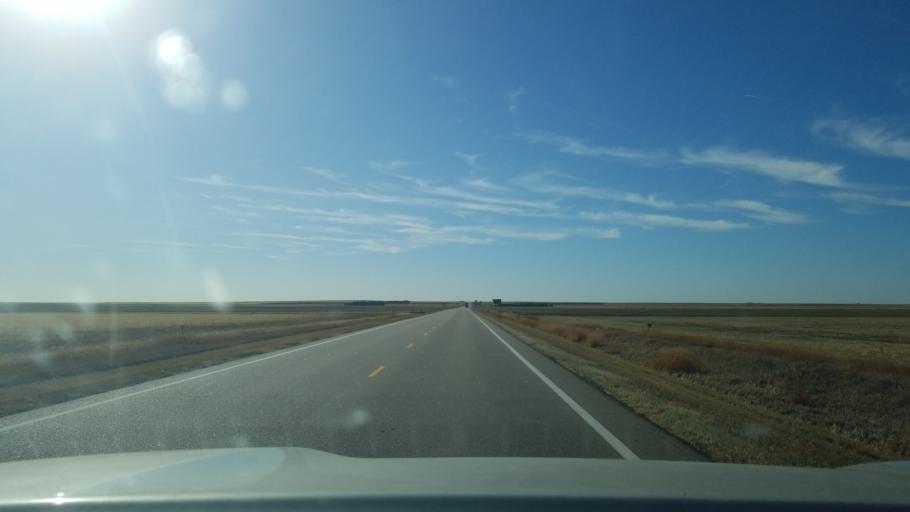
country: US
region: Kansas
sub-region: Ness County
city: Ness City
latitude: 38.3802
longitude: -99.8981
